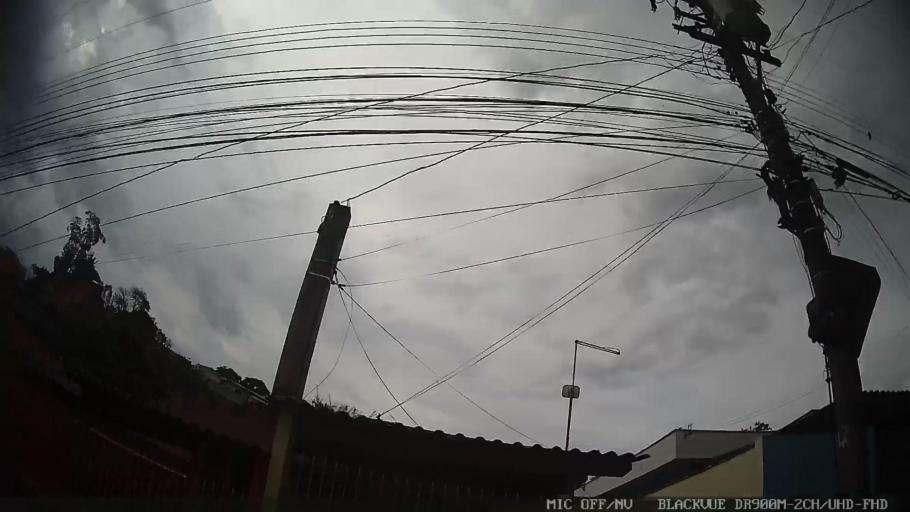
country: BR
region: Sao Paulo
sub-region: Itatiba
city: Itatiba
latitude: -23.0092
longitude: -46.8351
